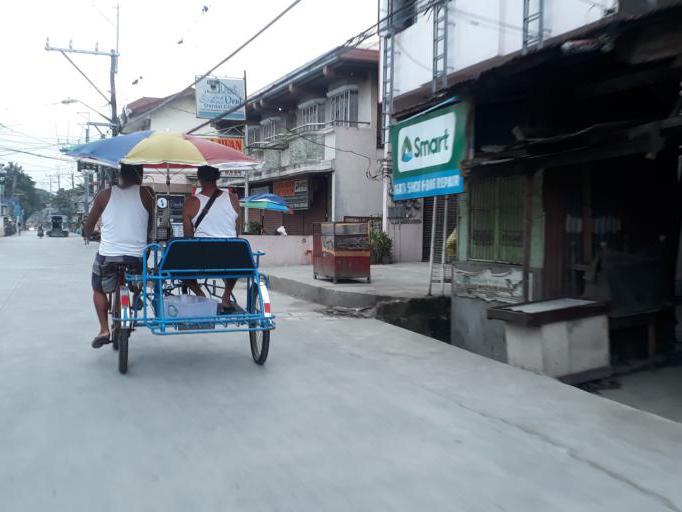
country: PH
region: Central Luzon
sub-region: Province of Bulacan
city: Obando
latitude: 14.7069
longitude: 120.9465
